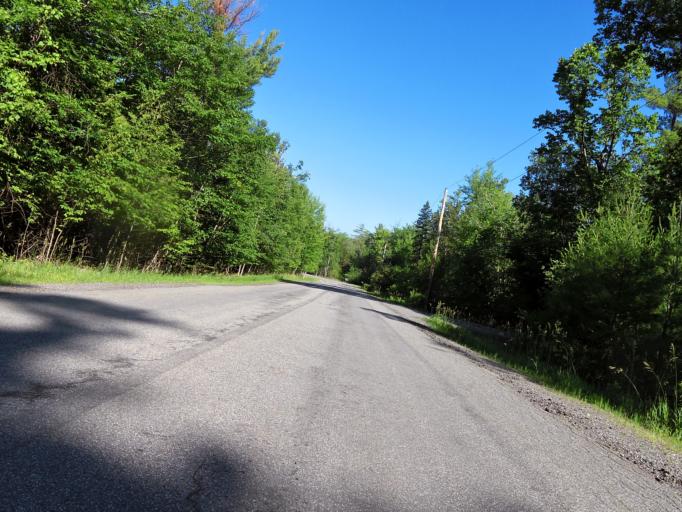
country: CA
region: Ontario
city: Arnprior
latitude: 45.4620
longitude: -76.2803
